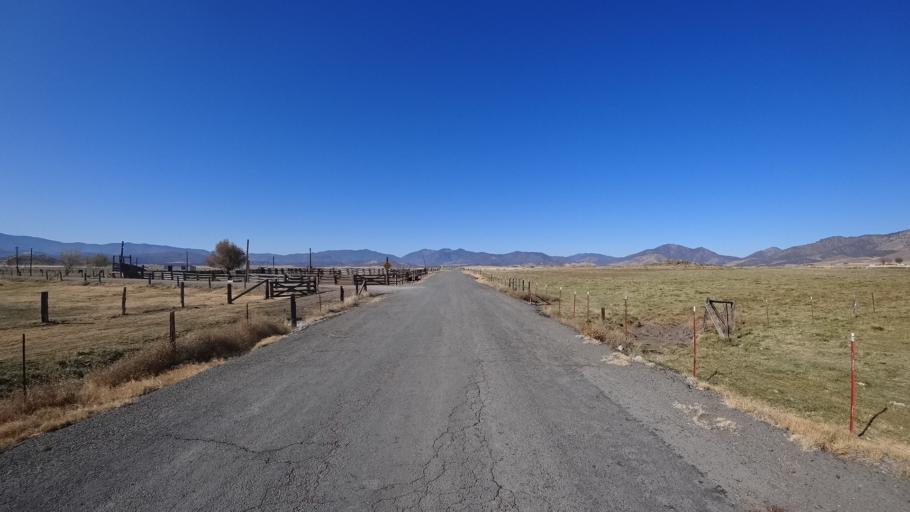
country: US
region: California
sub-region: Siskiyou County
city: Montague
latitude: 41.7420
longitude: -122.5267
